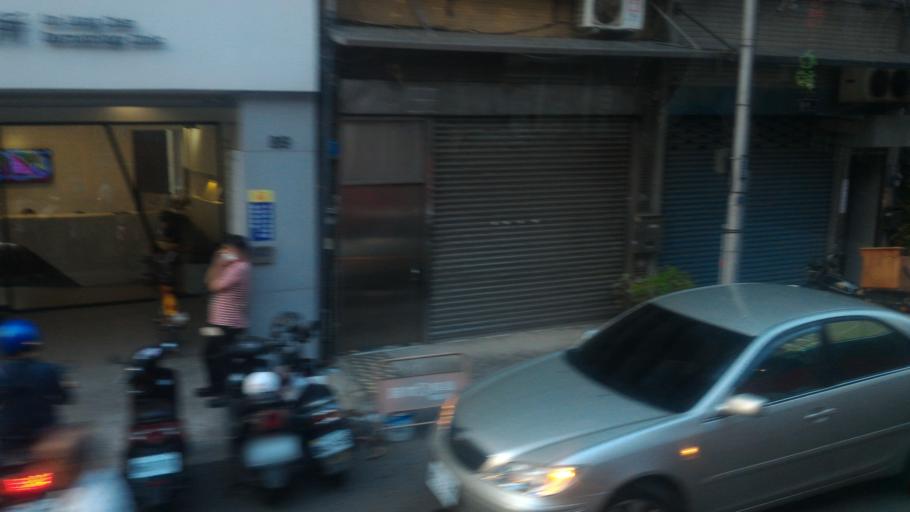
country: TW
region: Taiwan
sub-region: Hsinchu
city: Hsinchu
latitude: 24.8073
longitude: 120.9763
